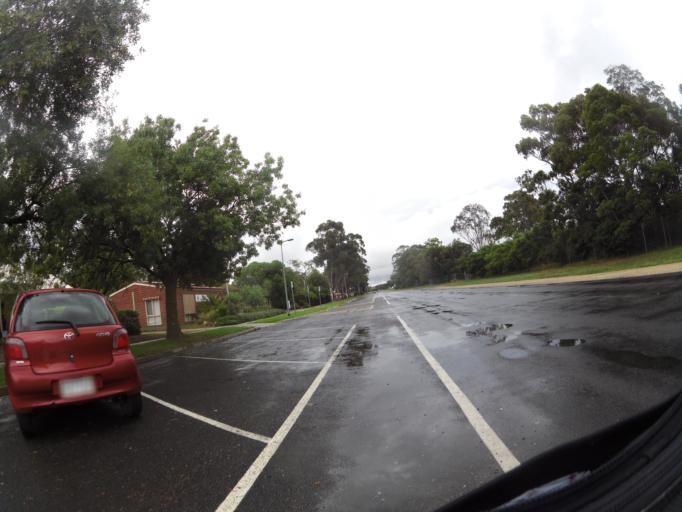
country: AU
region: Victoria
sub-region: East Gippsland
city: Bairnsdale
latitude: -37.8290
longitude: 147.6295
